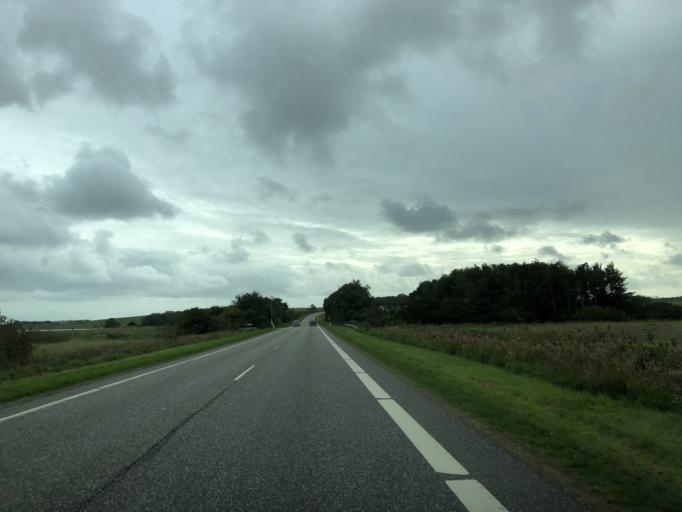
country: DK
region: North Denmark
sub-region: Thisted Kommune
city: Hurup
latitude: 56.7848
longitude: 8.4673
